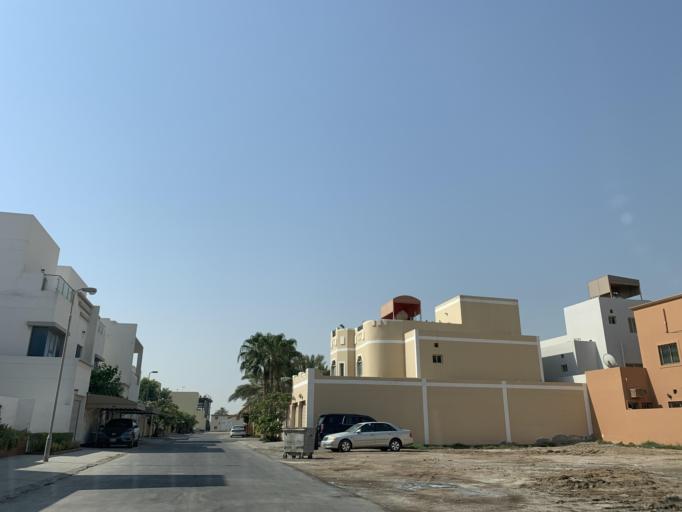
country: BH
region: Northern
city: Madinat `Isa
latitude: 26.1922
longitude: 50.5109
